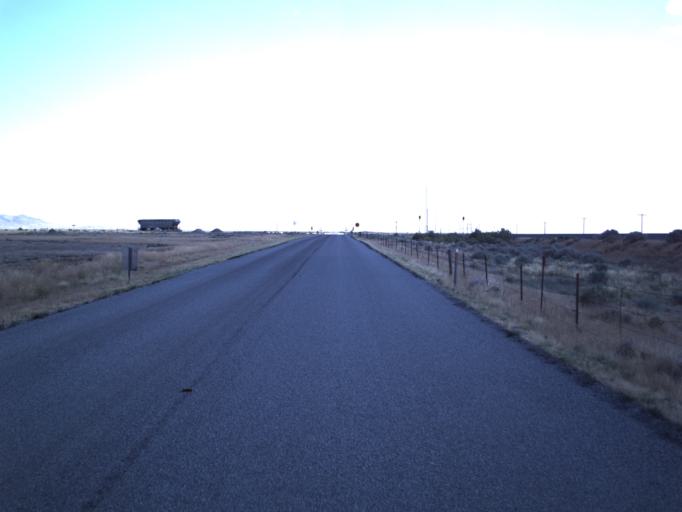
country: US
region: Utah
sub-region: Millard County
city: Delta
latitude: 38.9349
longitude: -112.8091
